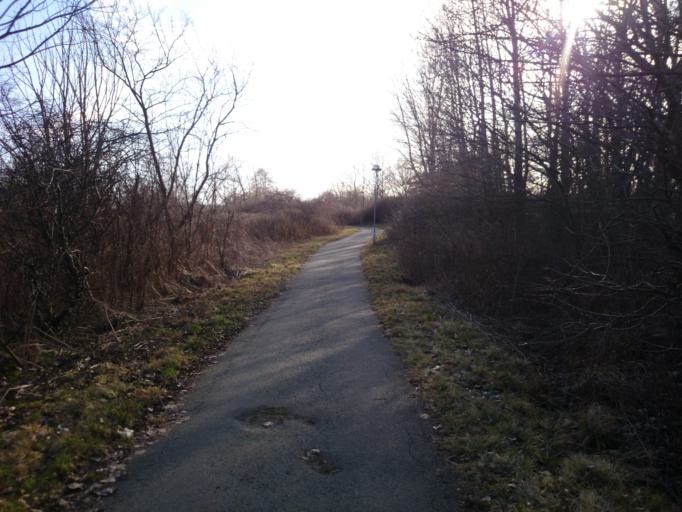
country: SE
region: Skane
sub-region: Simrishamns Kommun
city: Simrishamn
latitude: 55.5285
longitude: 14.3516
